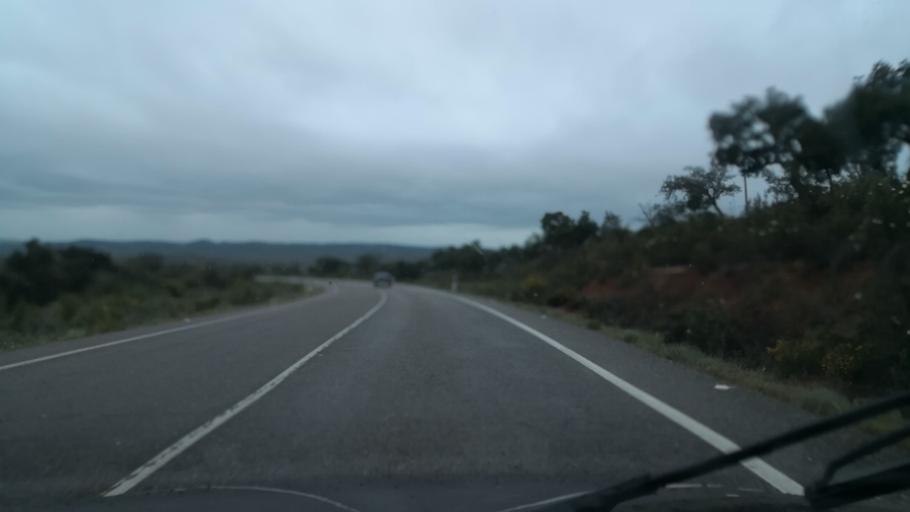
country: ES
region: Extremadura
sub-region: Provincia de Badajoz
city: Puebla de Obando
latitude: 39.1640
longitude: -6.6379
